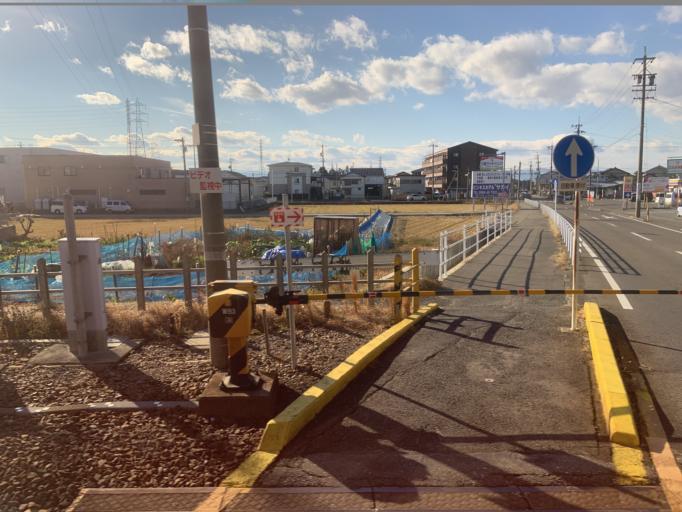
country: JP
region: Aichi
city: Ichinomiya
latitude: 35.2824
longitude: 136.8067
